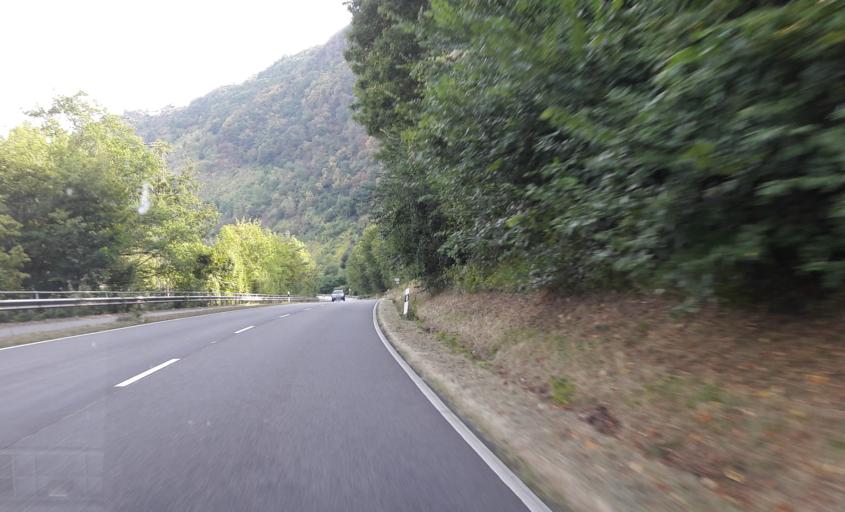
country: DE
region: Rheinland-Pfalz
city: Traben-Trarbach
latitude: 49.9505
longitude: 7.1282
